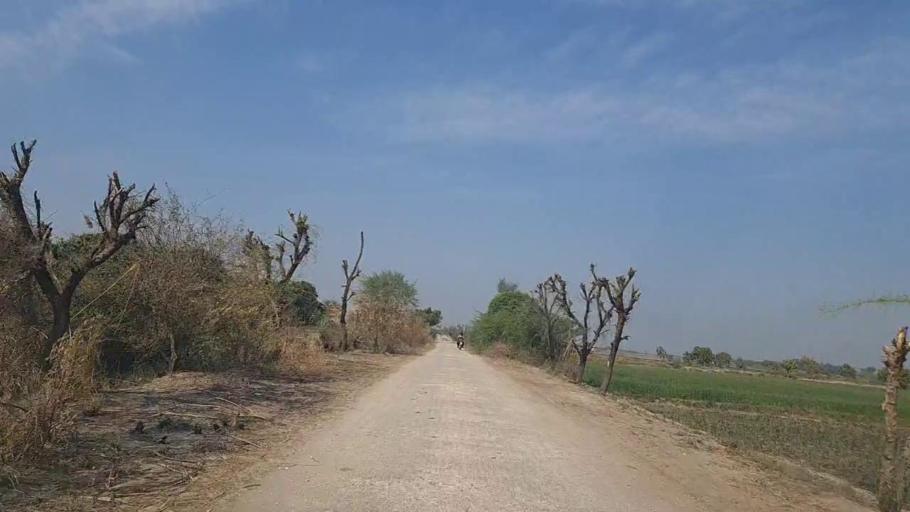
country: PK
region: Sindh
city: Mirpur Khas
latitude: 25.4904
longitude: 68.9205
